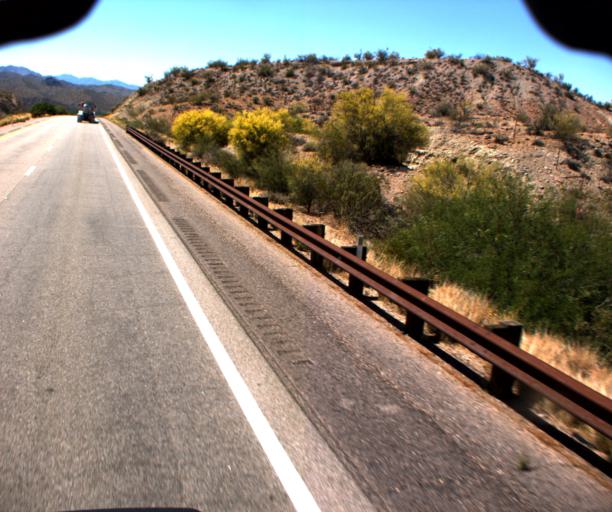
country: US
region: Arizona
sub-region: Yavapai County
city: Bagdad
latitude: 34.6339
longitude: -113.5509
